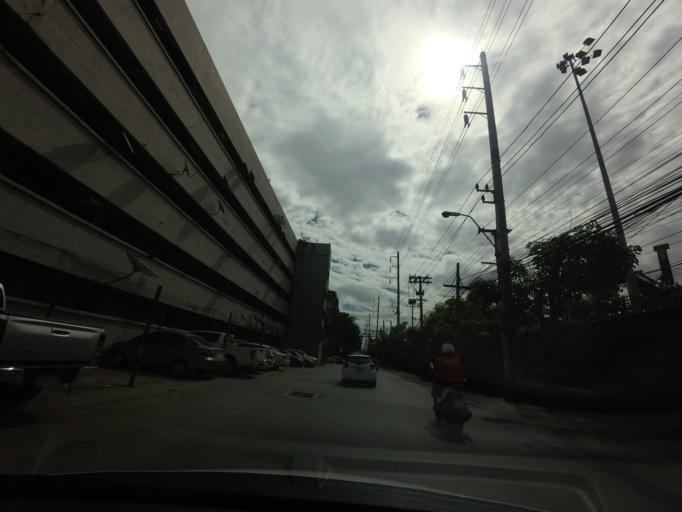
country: TH
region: Bangkok
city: Phra Khanong
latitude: 13.6942
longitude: 100.5901
